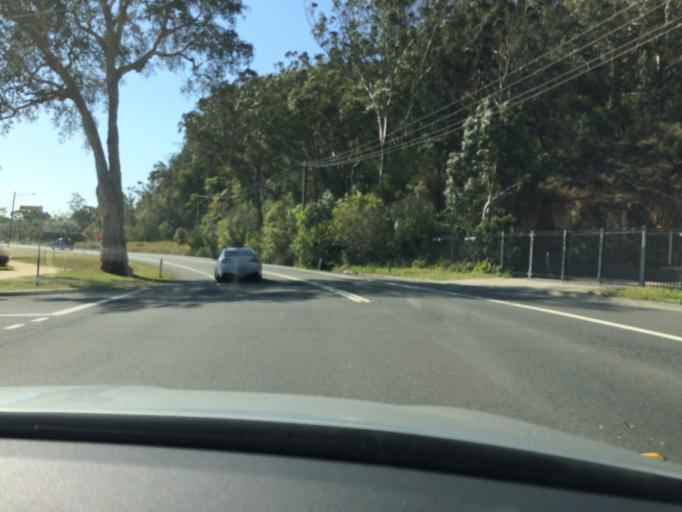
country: AU
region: New South Wales
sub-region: Gosford Shire
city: Ettalong Beach
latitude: -33.5057
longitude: 151.3315
